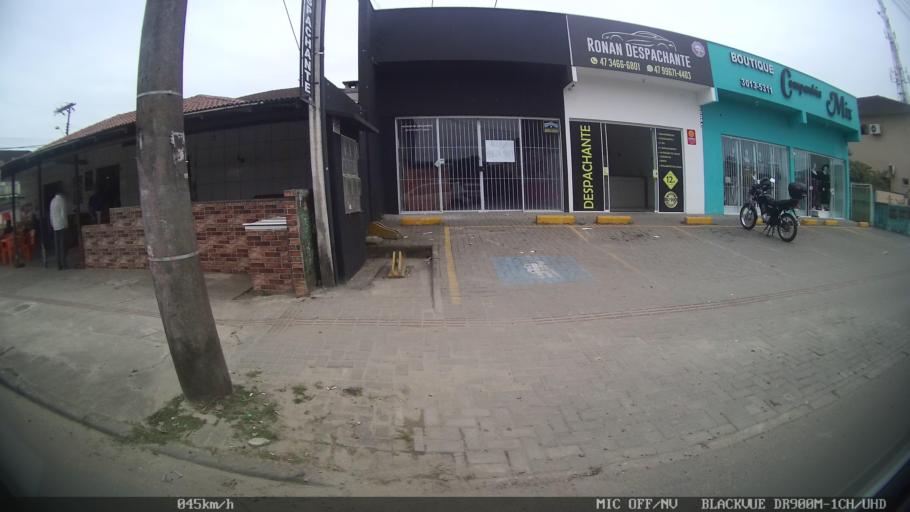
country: BR
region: Santa Catarina
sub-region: Joinville
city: Joinville
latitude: -26.3282
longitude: -48.8174
